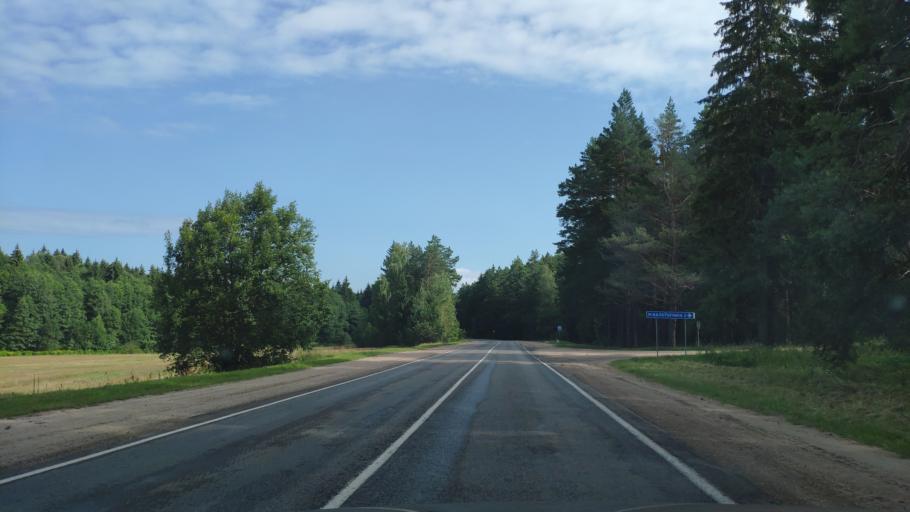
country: BY
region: Minsk
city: Zaslawye
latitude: 53.9702
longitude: 27.2473
